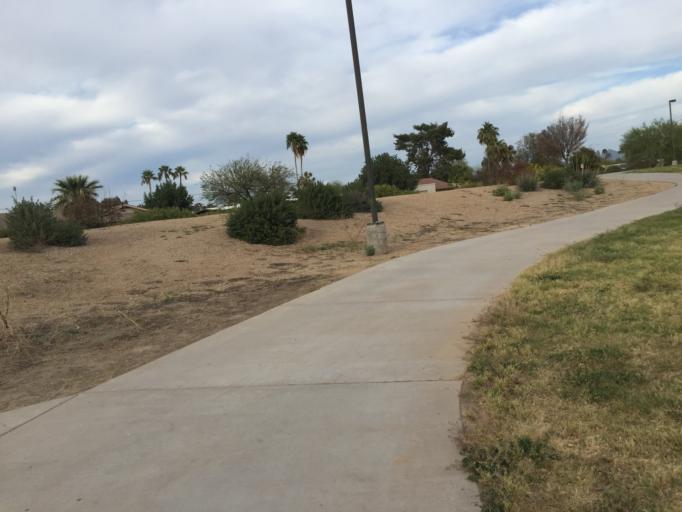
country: US
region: Arizona
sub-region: Maricopa County
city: Paradise Valley
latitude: 33.5749
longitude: -112.0101
